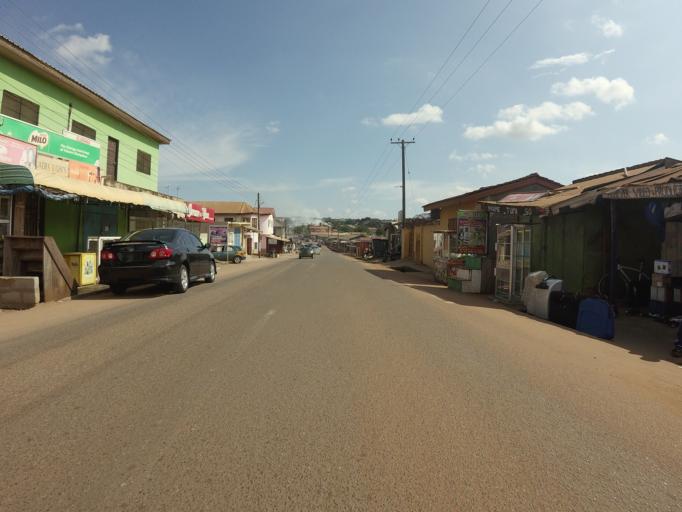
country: GH
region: Greater Accra
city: Medina Estates
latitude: 5.6752
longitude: -0.1818
